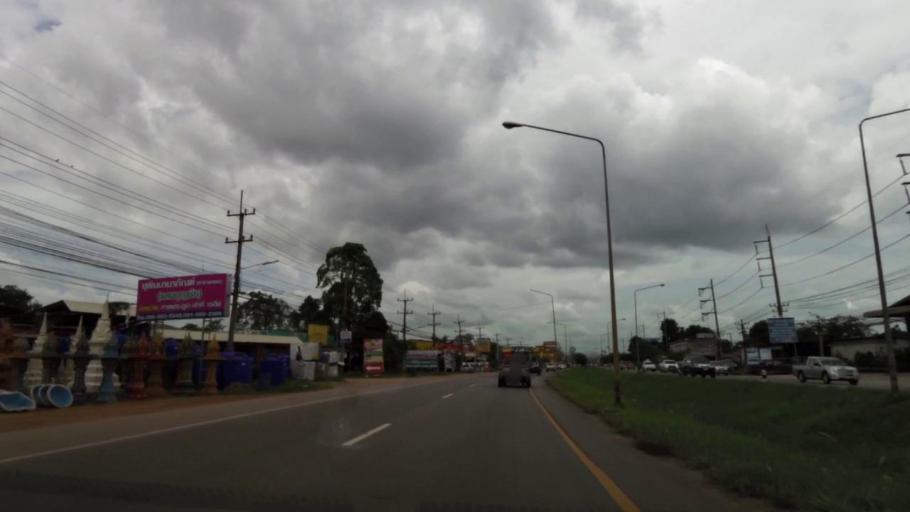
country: TH
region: Rayong
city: Klaeng
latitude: 12.7841
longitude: 101.6566
